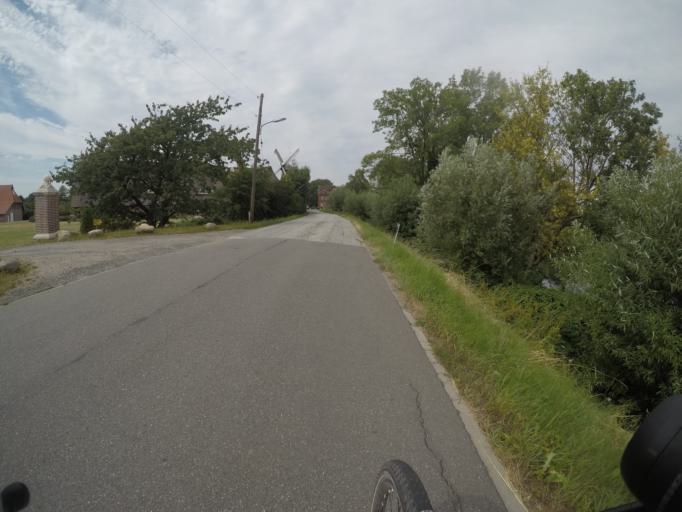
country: DE
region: Hamburg
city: Bergedorf
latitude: 53.4659
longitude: 10.1727
